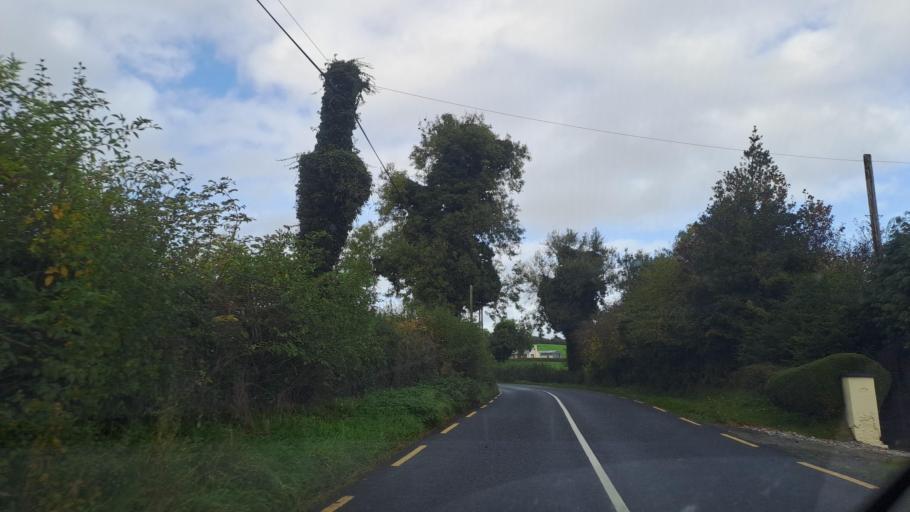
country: IE
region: Ulster
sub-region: County Monaghan
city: Carrickmacross
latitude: 53.9150
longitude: -6.7083
